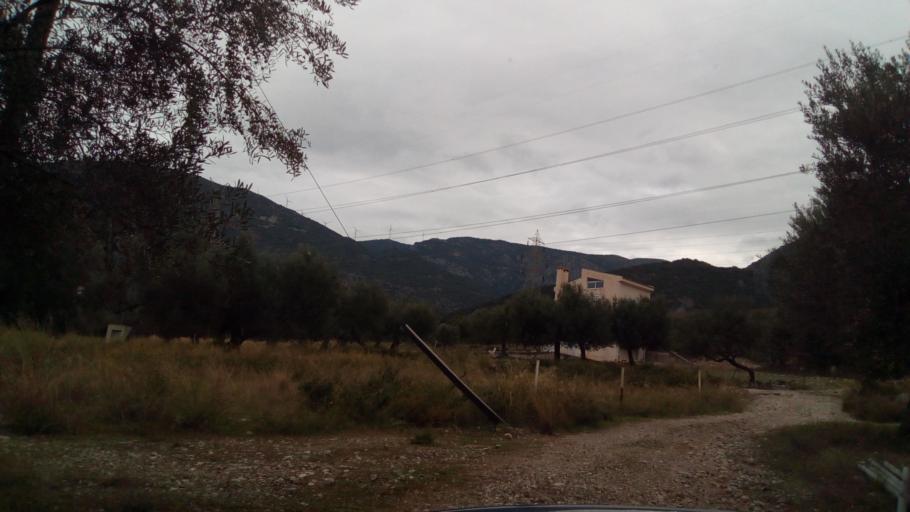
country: GR
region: West Greece
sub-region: Nomos Achaias
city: Kamarai
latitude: 38.3898
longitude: 22.0676
